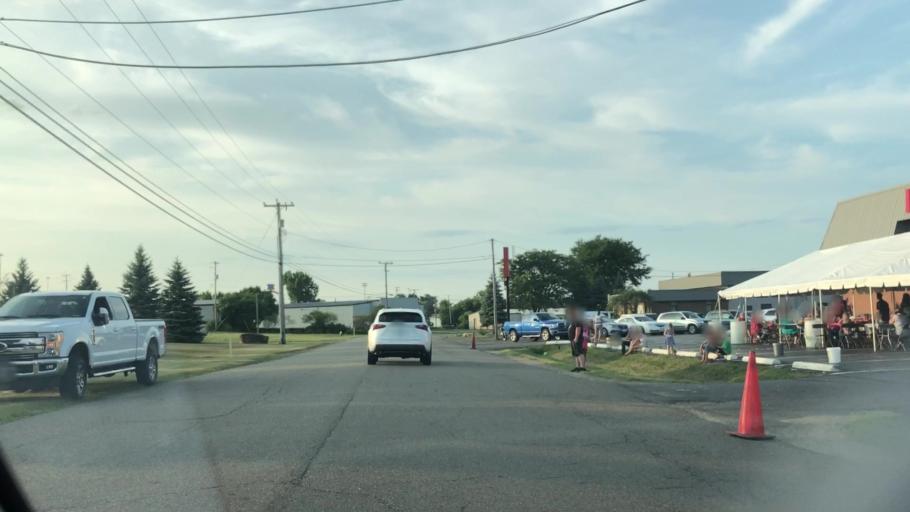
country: US
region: Ohio
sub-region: Stark County
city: North Canton
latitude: 40.8744
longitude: -81.4286
